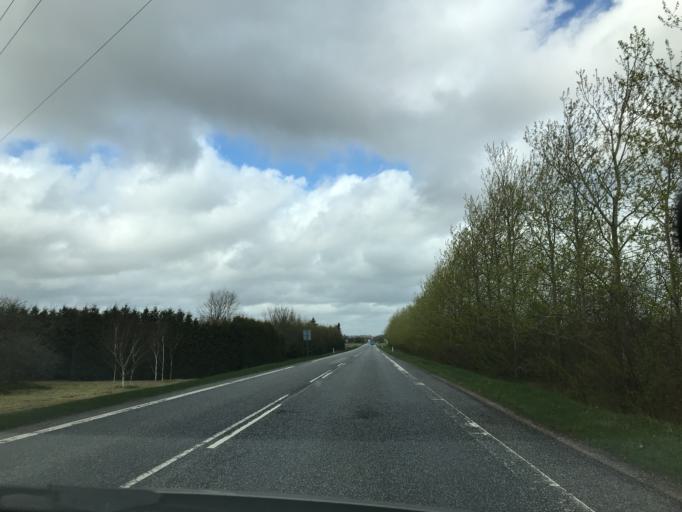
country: DK
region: Central Jutland
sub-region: Viborg Kommune
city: Stoholm
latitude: 56.3932
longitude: 8.9973
